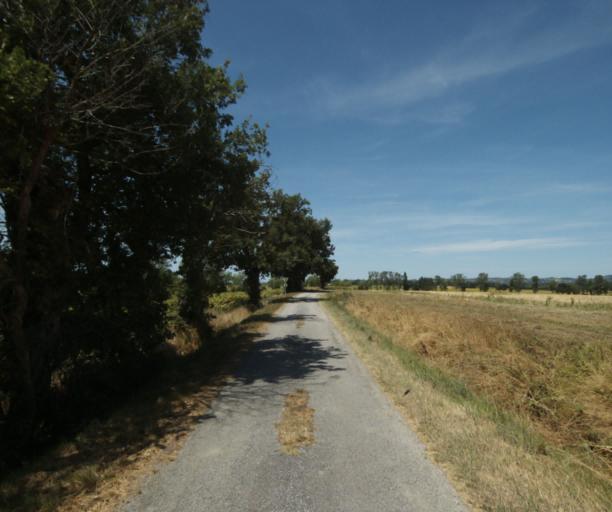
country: FR
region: Midi-Pyrenees
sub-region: Departement de la Haute-Garonne
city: Revel
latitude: 43.4905
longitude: 2.0366
